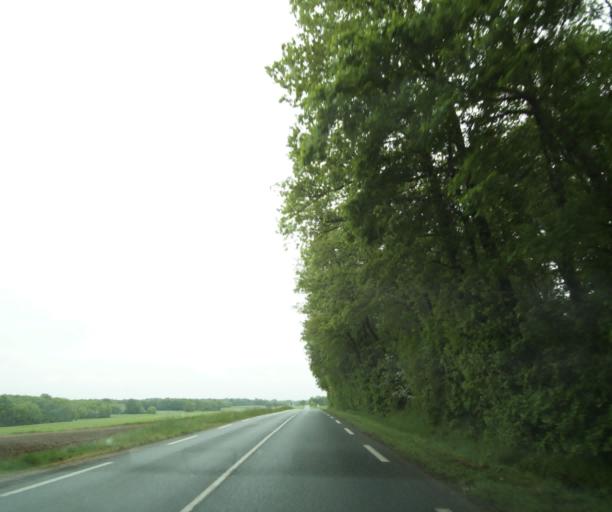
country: FR
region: Poitou-Charentes
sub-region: Departement de la Charente-Maritime
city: Saint-Georges-des-Coteaux
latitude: 45.7454
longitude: -0.7148
